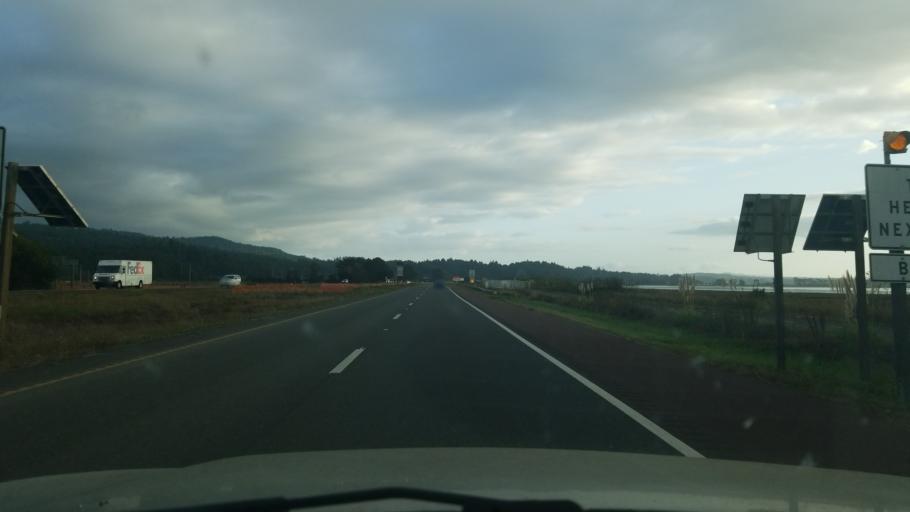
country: US
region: California
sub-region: Humboldt County
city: Bayside
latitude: 40.8418
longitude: -124.0822
